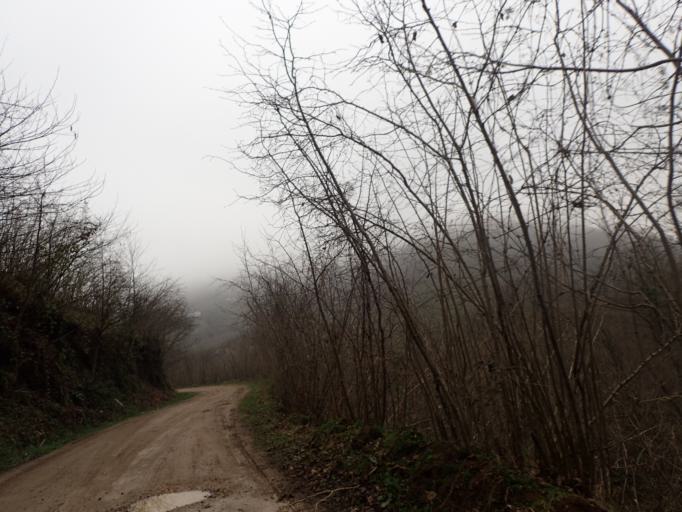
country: TR
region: Ordu
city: Camas
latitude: 40.9187
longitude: 37.5567
